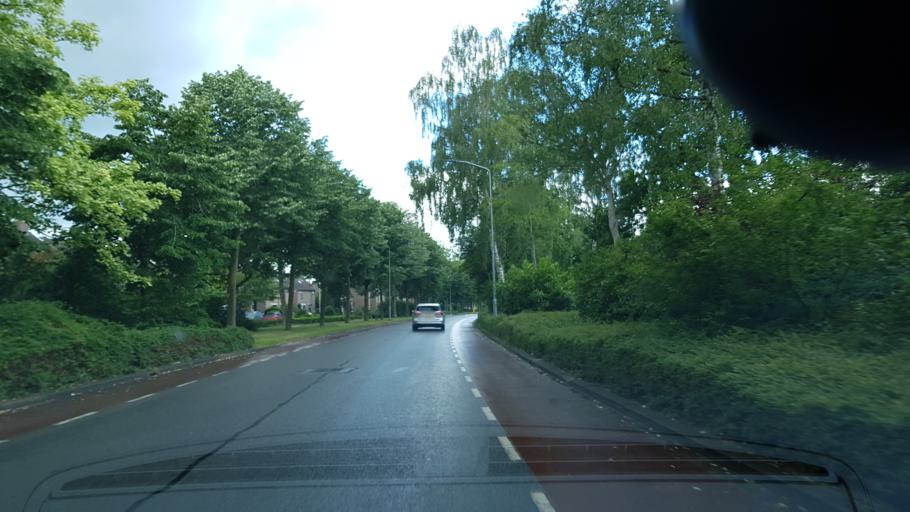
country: NL
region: Gelderland
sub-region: Gemeente Ermelo
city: Ermelo
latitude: 52.2968
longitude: 5.6021
